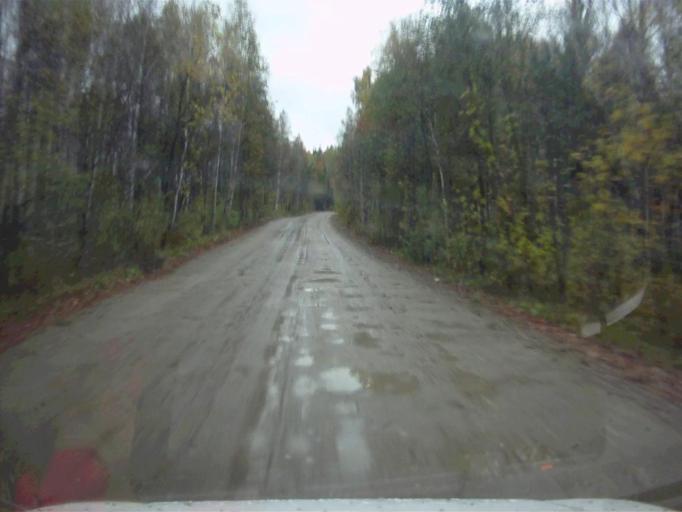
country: RU
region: Chelyabinsk
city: Kyshtym
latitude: 55.8327
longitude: 60.4863
